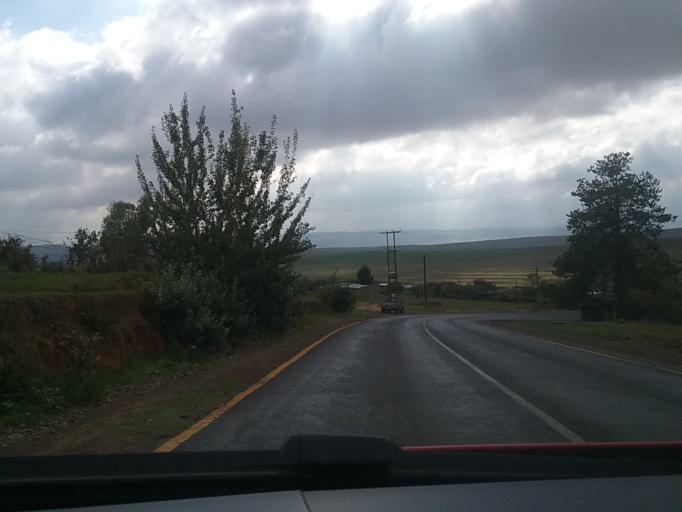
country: LS
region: Berea
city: Teyateyaneng
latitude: -29.1627
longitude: 27.7754
